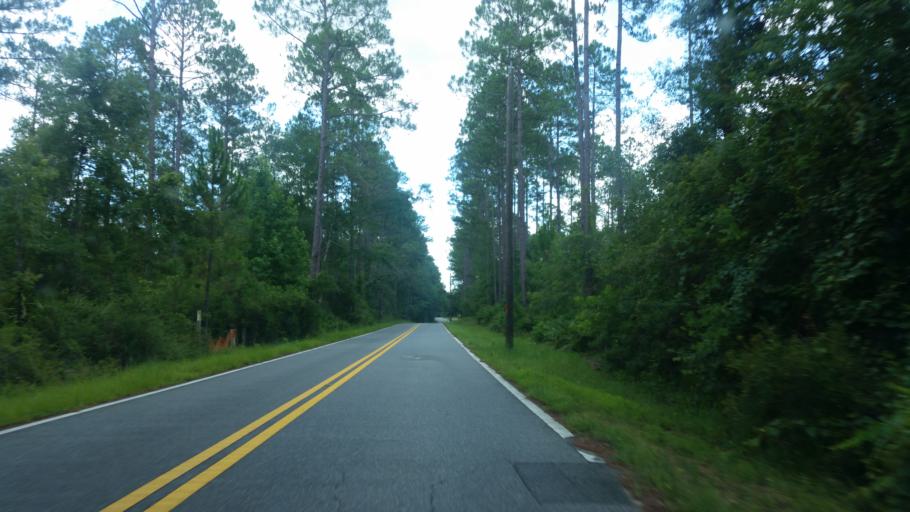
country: US
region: Florida
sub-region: Leon County
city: Woodville
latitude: 30.2861
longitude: -84.1571
